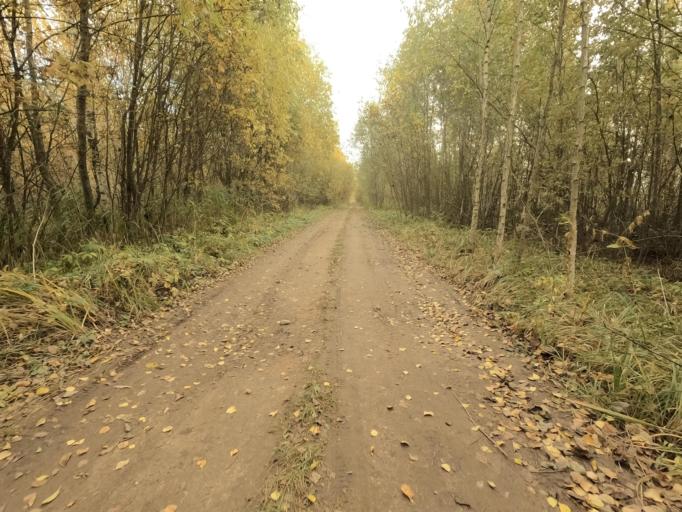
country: RU
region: Novgorod
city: Pankovka
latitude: 58.8757
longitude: 30.8737
